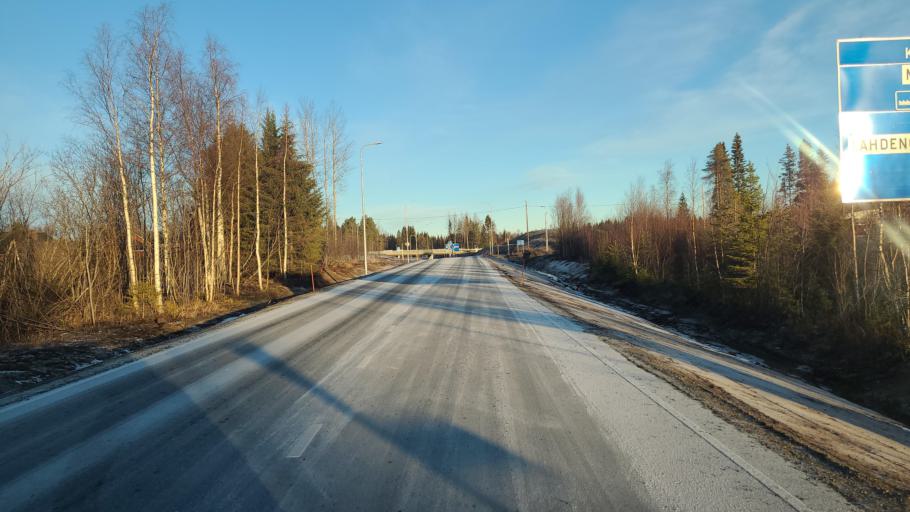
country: FI
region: Lapland
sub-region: Kemi-Tornio
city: Kemi
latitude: 65.6761
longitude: 24.7436
